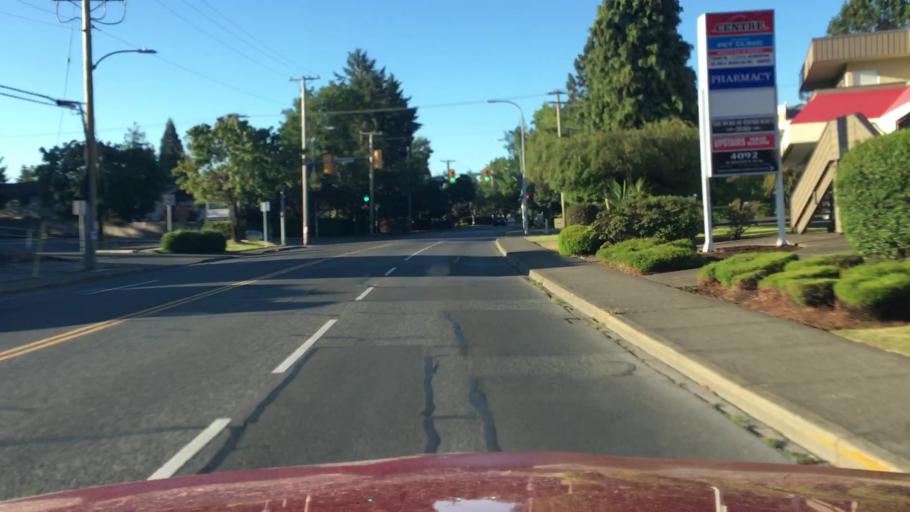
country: CA
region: British Columbia
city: Oak Bay
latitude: 48.4767
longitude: -123.3332
